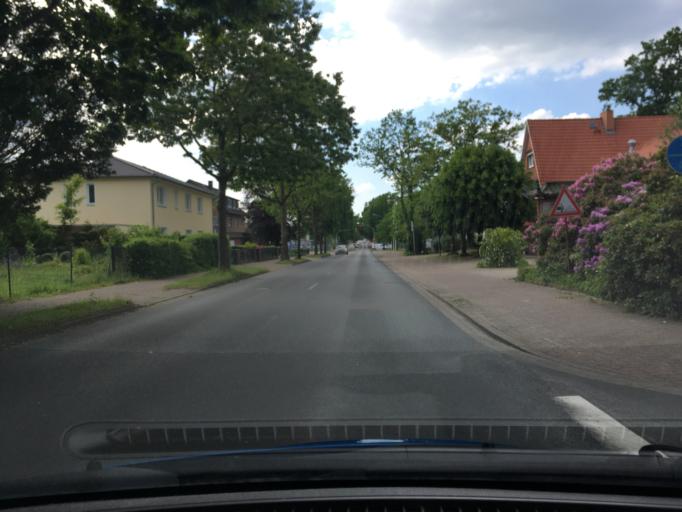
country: DE
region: Lower Saxony
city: Tostedt
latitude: 53.2667
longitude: 9.7294
